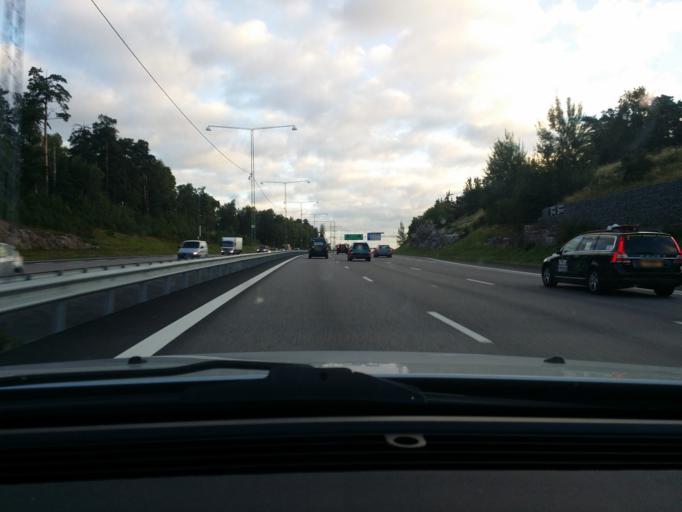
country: SE
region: Stockholm
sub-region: Upplands Vasby Kommun
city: Upplands Vaesby
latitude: 59.4886
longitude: 17.9191
